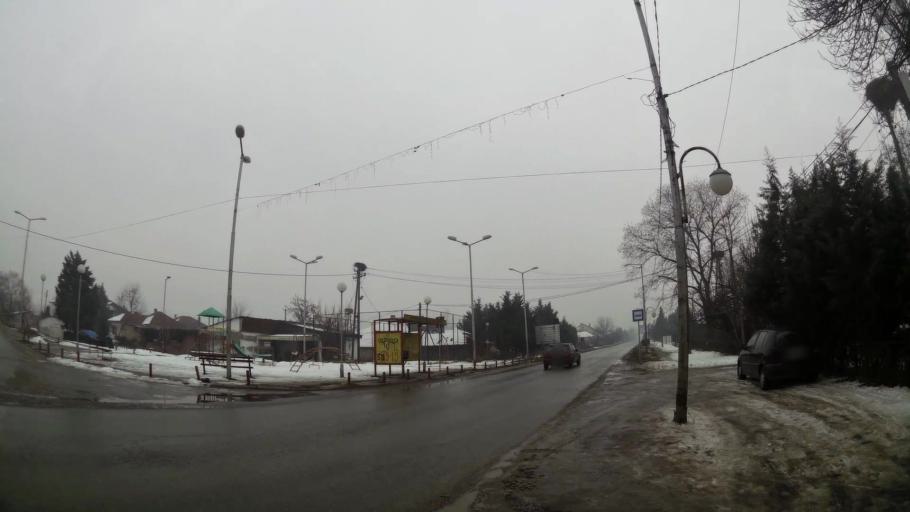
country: MK
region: Petrovec
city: Petrovec
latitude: 41.9256
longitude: 21.6305
